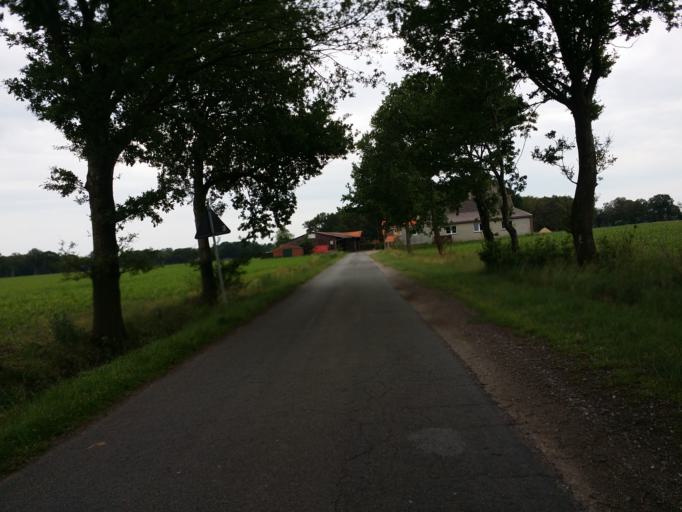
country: DE
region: Lower Saxony
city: Wiefelstede
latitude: 53.3122
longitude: 8.0518
